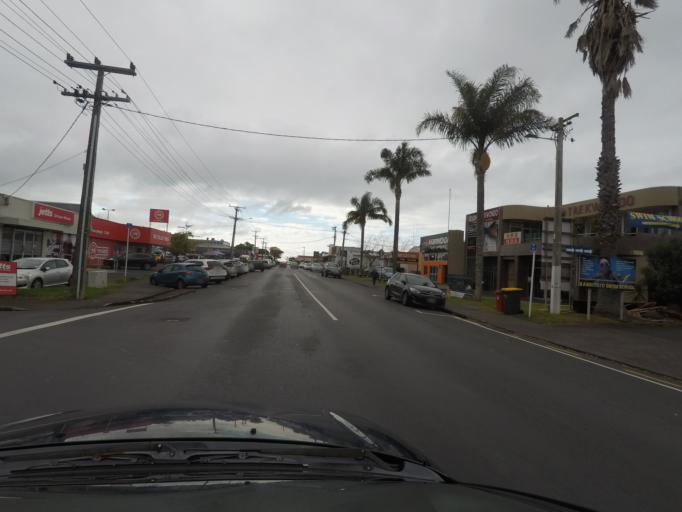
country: NZ
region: Auckland
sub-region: Auckland
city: Rothesay Bay
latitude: -36.7168
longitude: 174.7454
